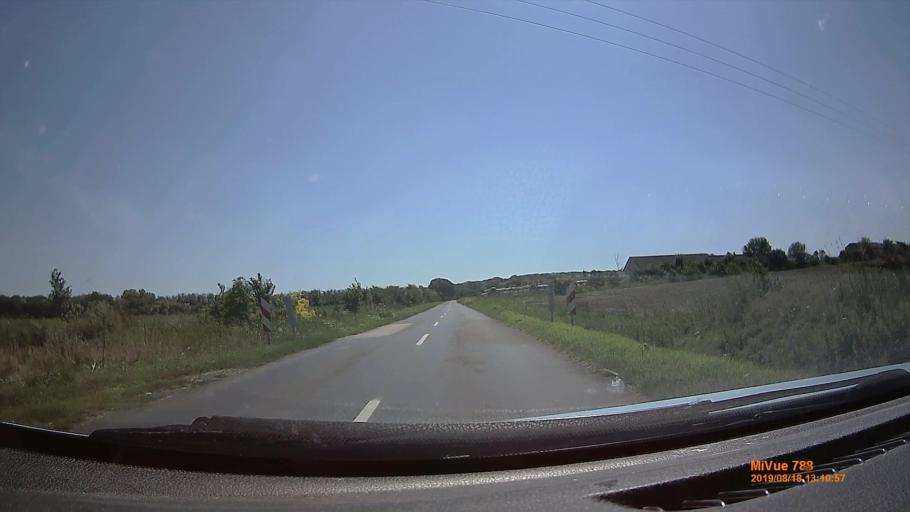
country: HU
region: Fejer
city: Kaloz
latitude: 46.9083
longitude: 18.5183
